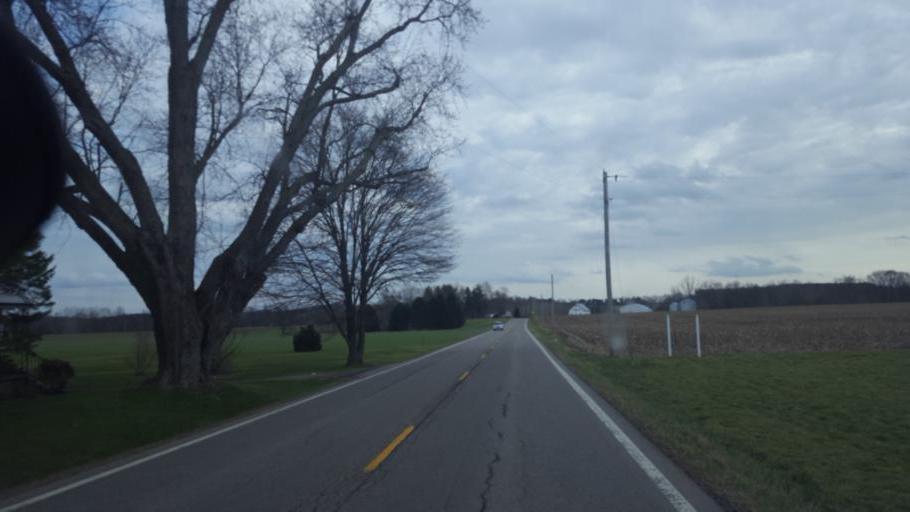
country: US
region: Ohio
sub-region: Richland County
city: Lexington
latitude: 40.6233
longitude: -82.5903
